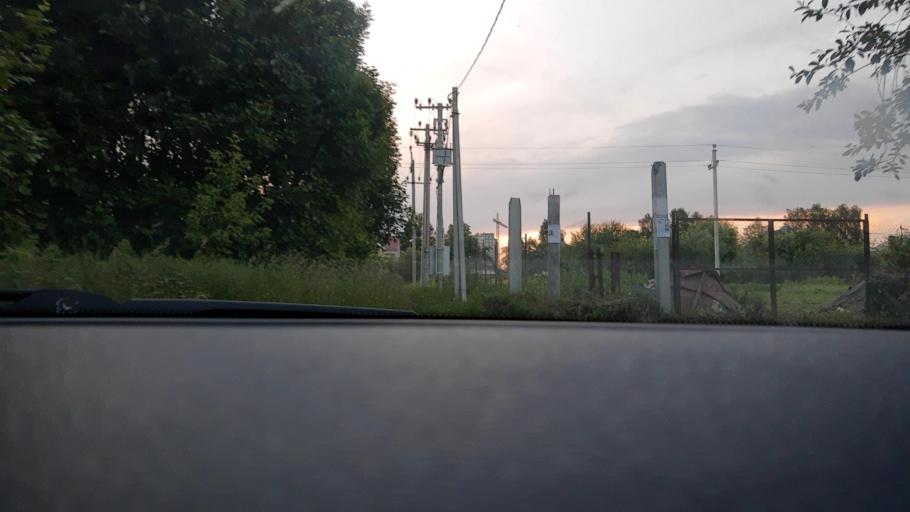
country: RU
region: Nizjnij Novgorod
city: Afonino
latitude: 56.2419
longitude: 44.0481
